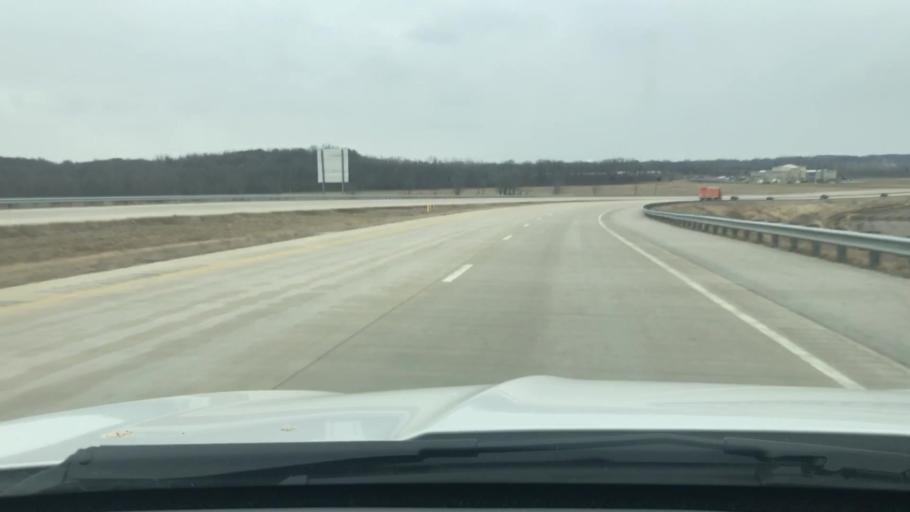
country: US
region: Indiana
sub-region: Cass County
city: Logansport
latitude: 40.7323
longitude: -86.3632
